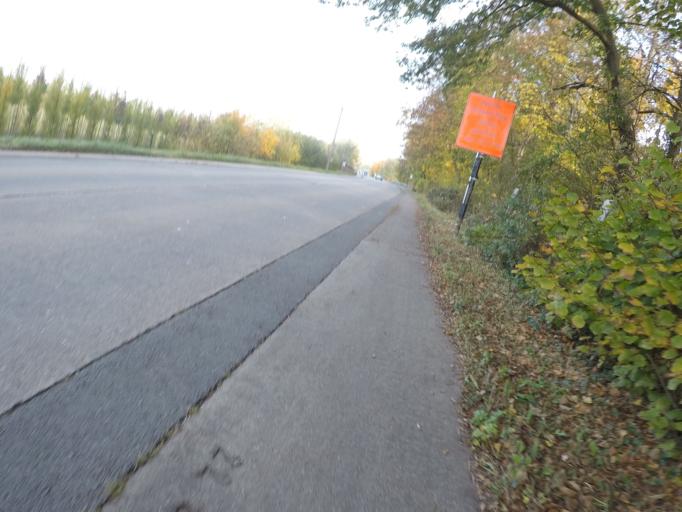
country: BE
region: Flanders
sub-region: Provincie Vlaams-Brabant
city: Begijnendijk
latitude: 50.9781
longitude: 4.7817
